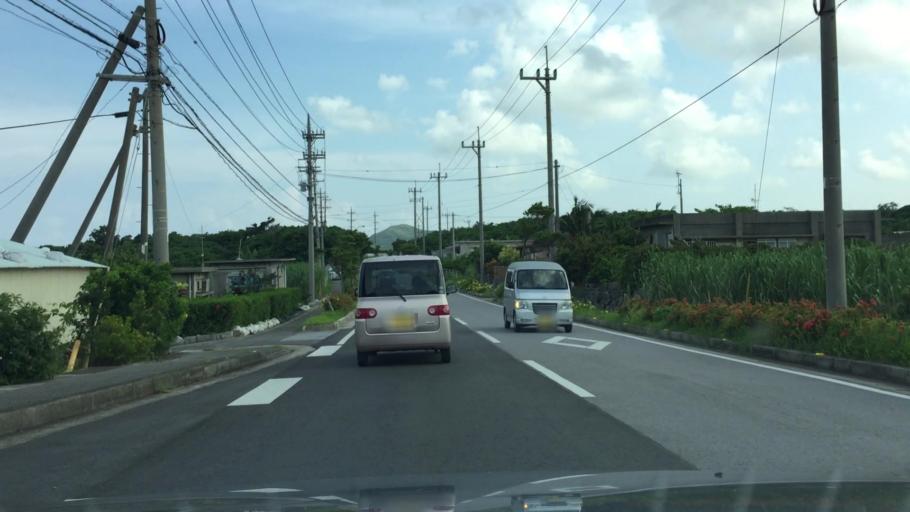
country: JP
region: Okinawa
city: Ishigaki
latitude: 24.4380
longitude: 124.2491
